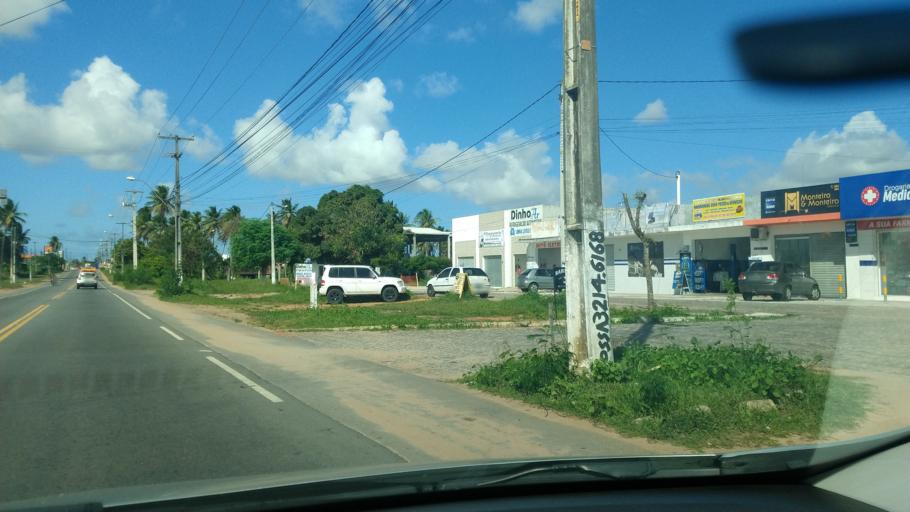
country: BR
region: Rio Grande do Norte
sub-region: Sao Goncalo Do Amarante
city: Sao Goncalo do Amarante
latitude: -5.7890
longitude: -35.3027
